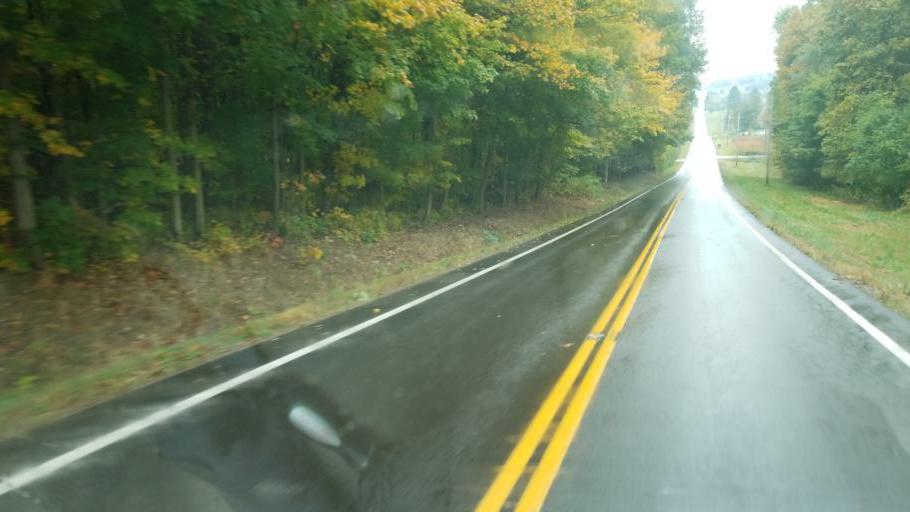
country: US
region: Ohio
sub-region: Richland County
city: Lincoln Heights
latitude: 40.6771
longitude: -82.3780
